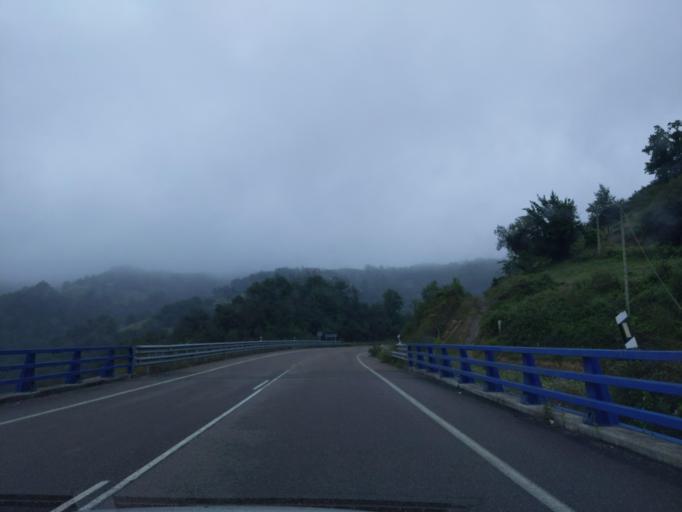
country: ES
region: Asturias
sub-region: Province of Asturias
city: Bimenes
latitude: 43.3184
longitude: -5.5970
